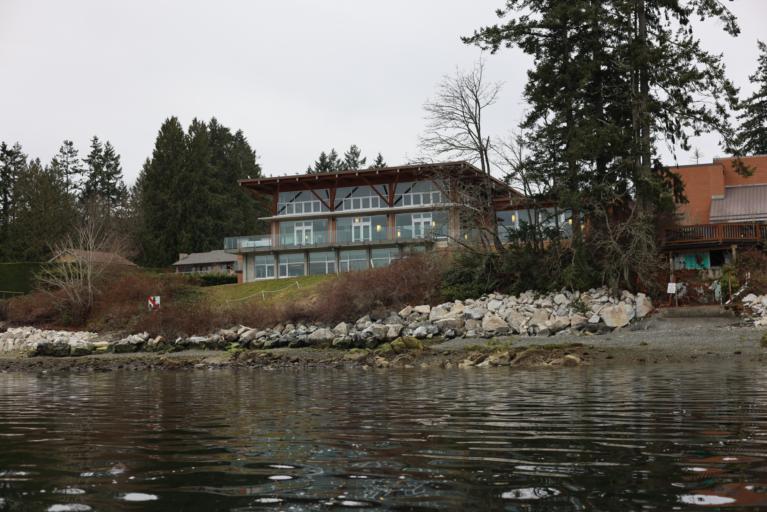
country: CA
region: British Columbia
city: North Saanich
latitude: 48.6518
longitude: -123.5519
